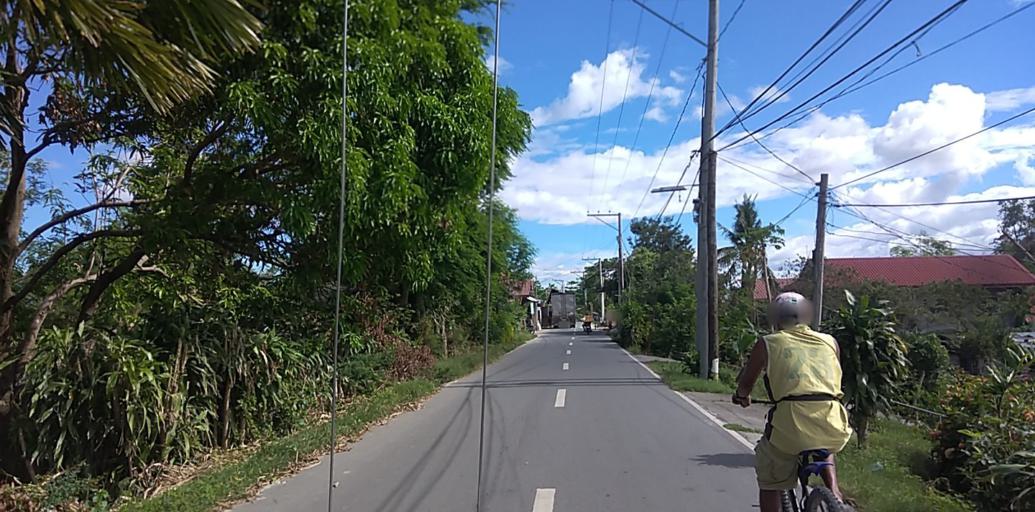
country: PH
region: Central Luzon
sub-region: Province of Pampanga
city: Arayat
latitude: 15.1354
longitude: 120.7866
